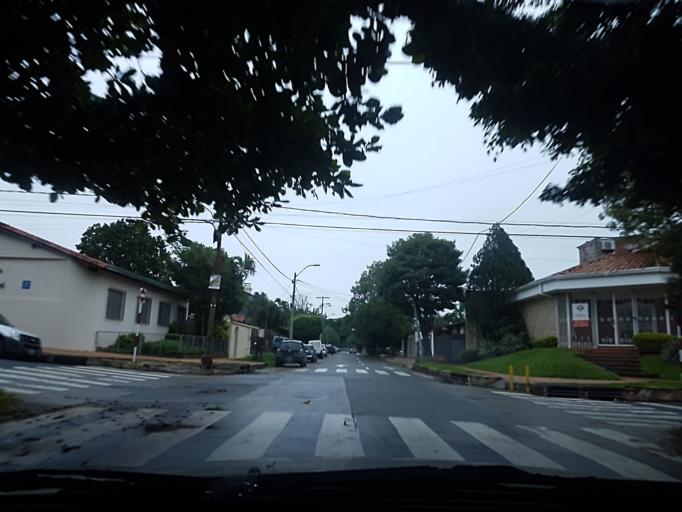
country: PY
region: Central
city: Fernando de la Mora
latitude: -25.3005
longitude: -57.5616
